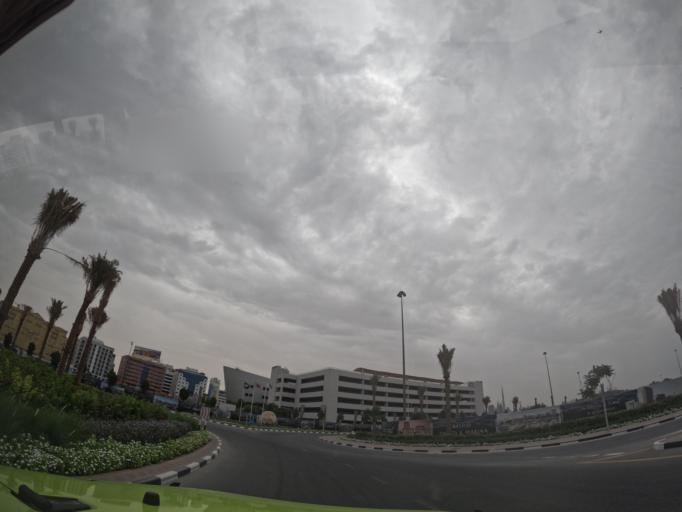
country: AE
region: Ash Shariqah
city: Sharjah
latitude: 25.2574
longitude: 55.2824
